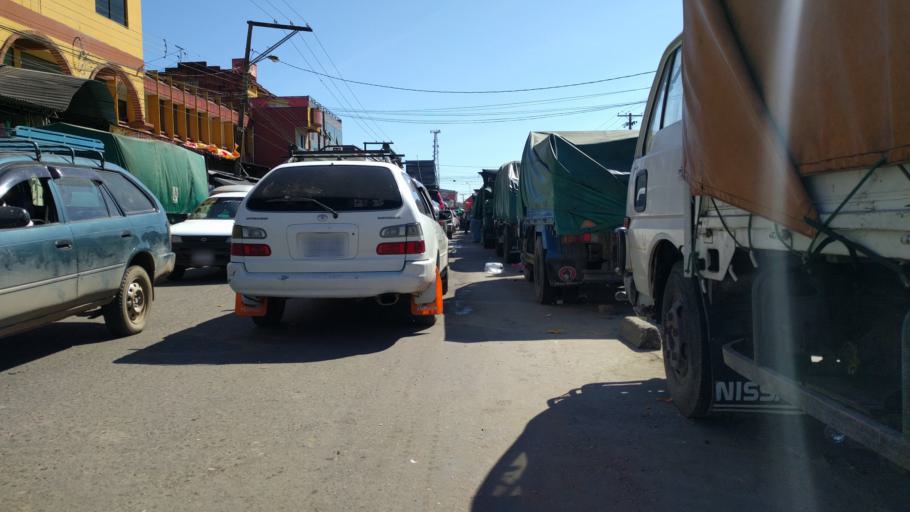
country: BO
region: Santa Cruz
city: Santa Cruz de la Sierra
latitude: -17.7967
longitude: -63.2052
